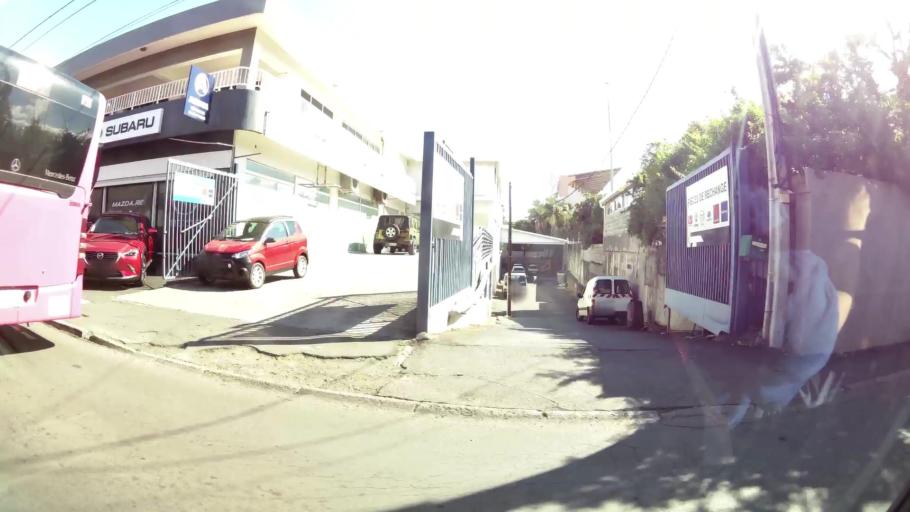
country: RE
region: Reunion
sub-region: Reunion
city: Saint-Pierre
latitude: -21.3397
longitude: 55.4693
